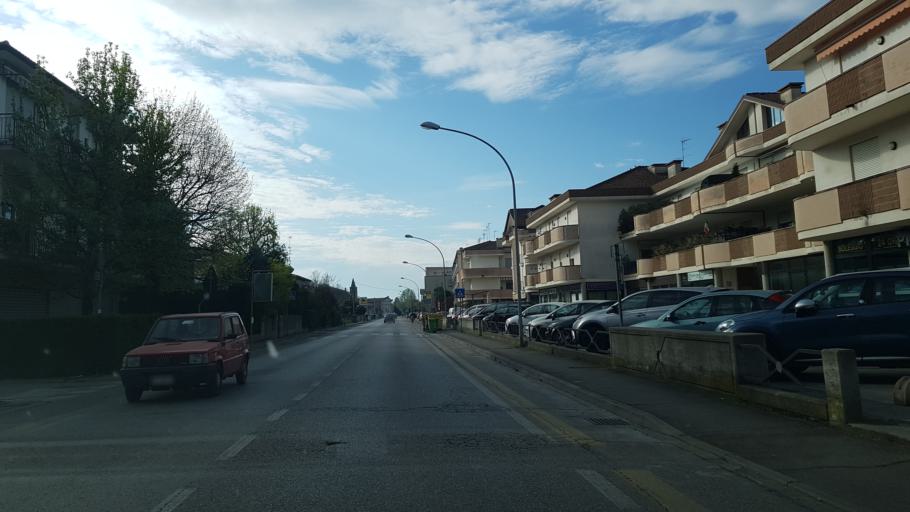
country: IT
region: Veneto
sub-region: Provincia di Rovigo
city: Rovigo
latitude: 45.0732
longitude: 11.7992
